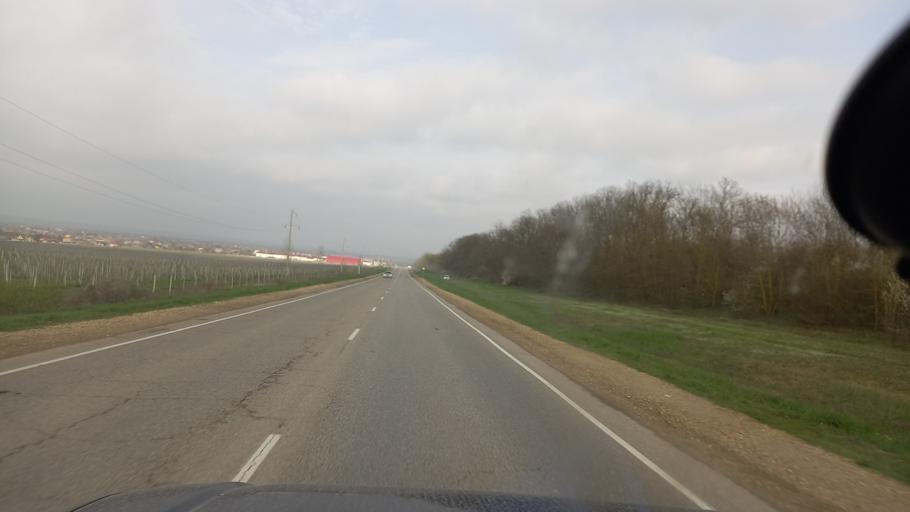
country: RU
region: Krasnodarskiy
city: Varenikovskaya
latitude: 45.1067
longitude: 37.6186
